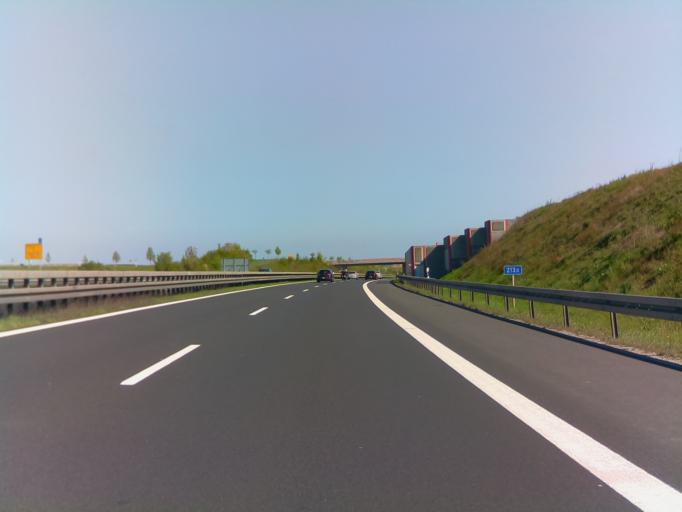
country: DE
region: Bavaria
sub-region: Regierungsbezirk Unterfranken
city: Euerbach
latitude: 50.0685
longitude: 10.1470
